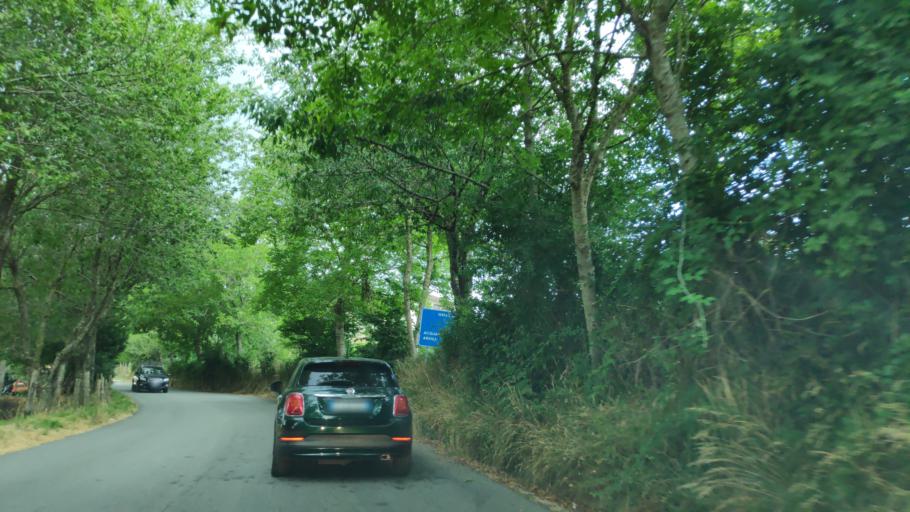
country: IT
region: Calabria
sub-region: Provincia di Vibo-Valentia
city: Mongiana
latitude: 38.5368
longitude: 16.3175
